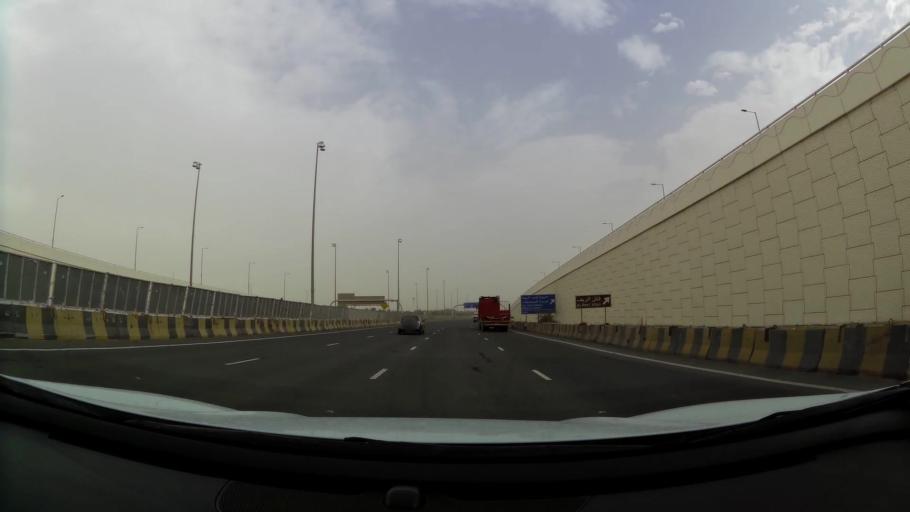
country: AE
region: Abu Dhabi
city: Abu Dhabi
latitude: 24.4652
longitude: 54.6296
